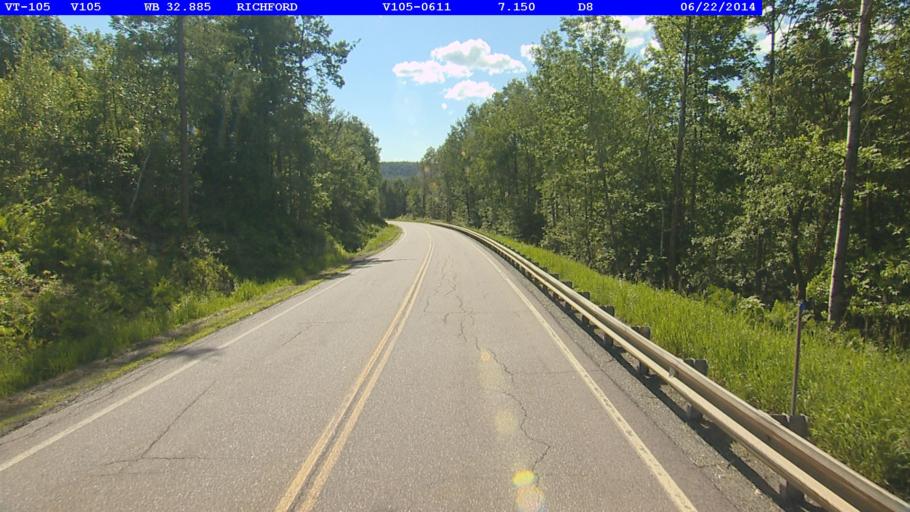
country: US
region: Vermont
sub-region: Franklin County
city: Richford
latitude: 45.0043
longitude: -72.5810
